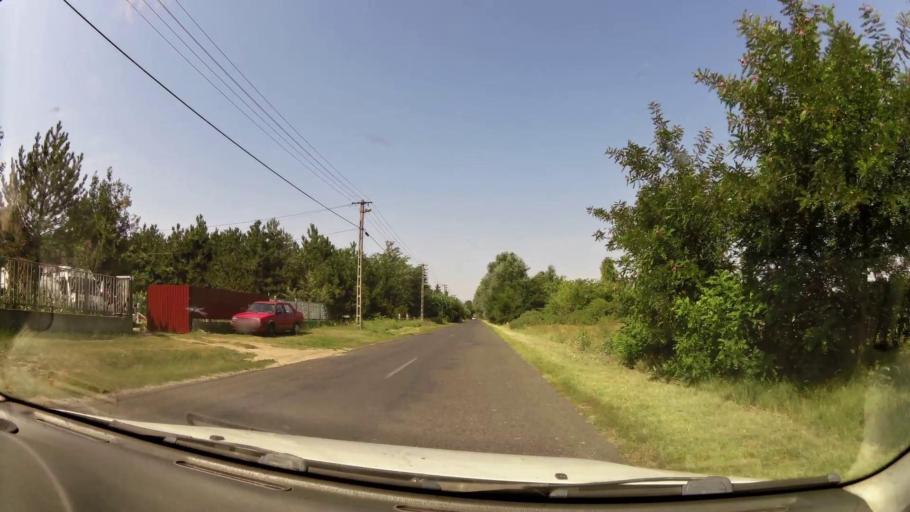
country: HU
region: Pest
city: Tapioszentmarton
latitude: 47.3404
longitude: 19.7889
